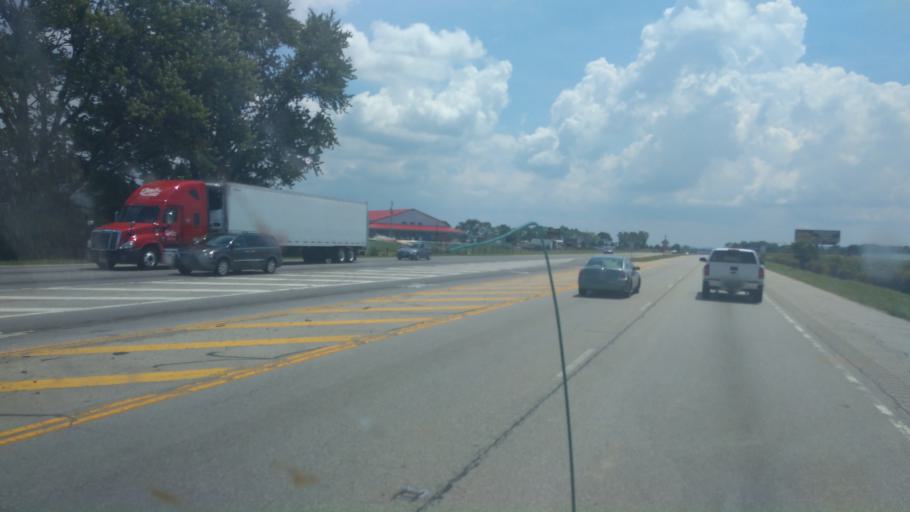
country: US
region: Ohio
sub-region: Fairfield County
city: Lancaster
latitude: 39.7715
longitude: -82.6819
